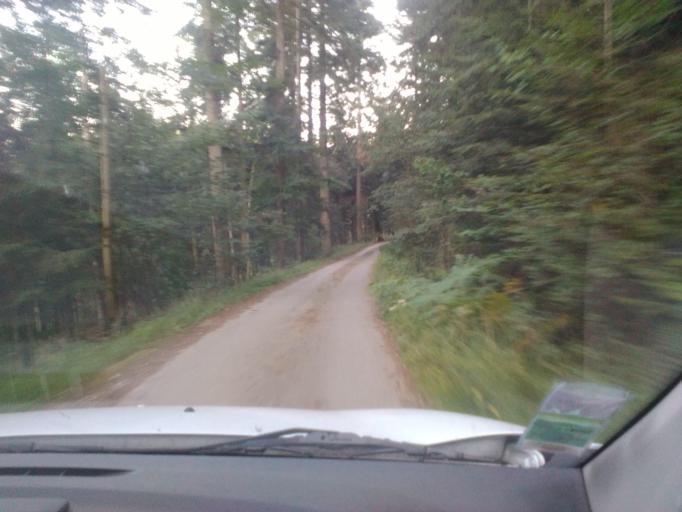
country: FR
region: Lorraine
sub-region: Departement des Vosges
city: Saint-Michel-sur-Meurthe
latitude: 48.3020
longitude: 6.9123
